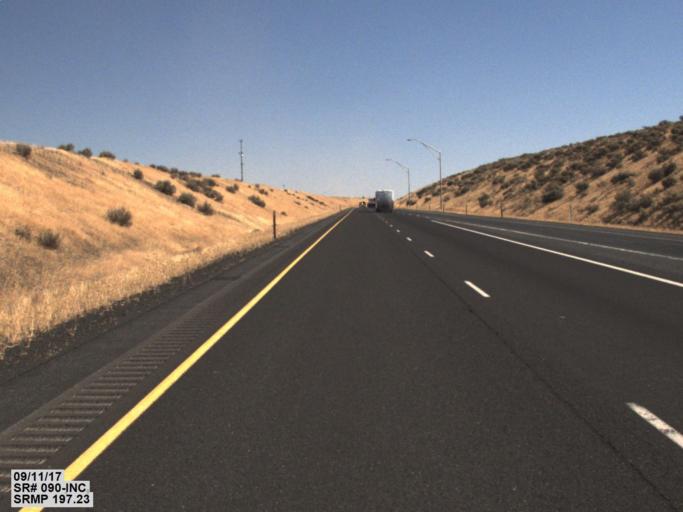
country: US
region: Washington
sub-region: Grant County
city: Warden
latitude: 47.0868
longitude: -118.8684
